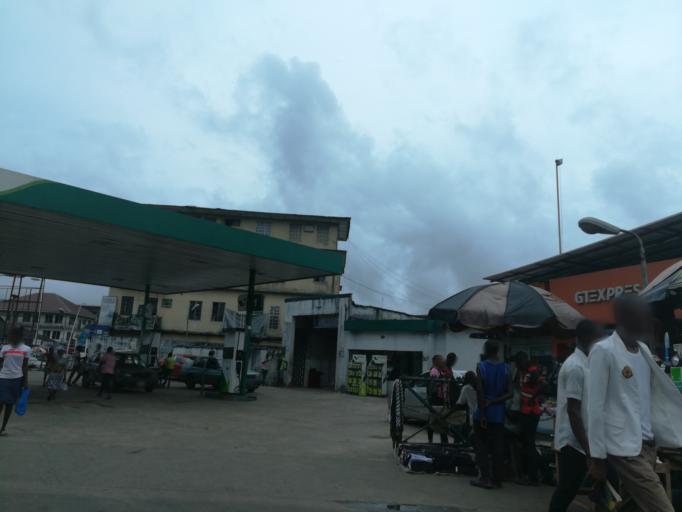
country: NG
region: Rivers
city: Port Harcourt
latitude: 4.7619
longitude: 7.0189
